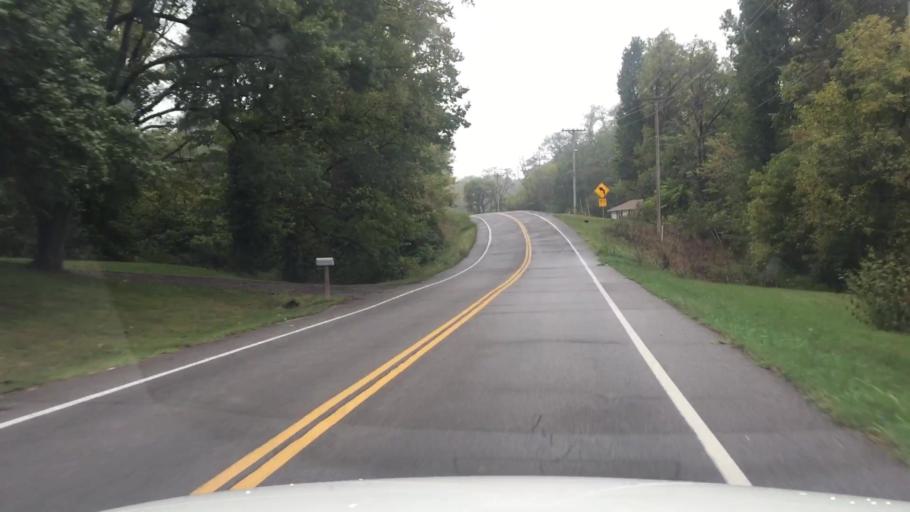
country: US
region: Missouri
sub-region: Boone County
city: Columbia
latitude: 38.8795
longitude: -92.4195
